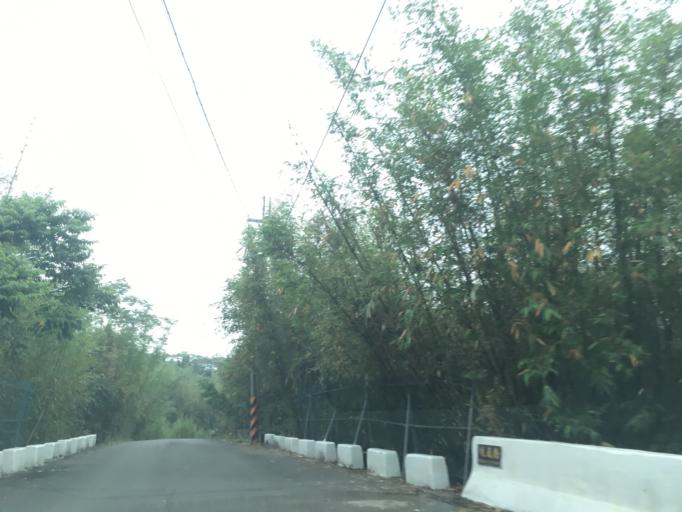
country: TW
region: Taiwan
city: Daxi
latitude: 24.8779
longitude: 121.3082
